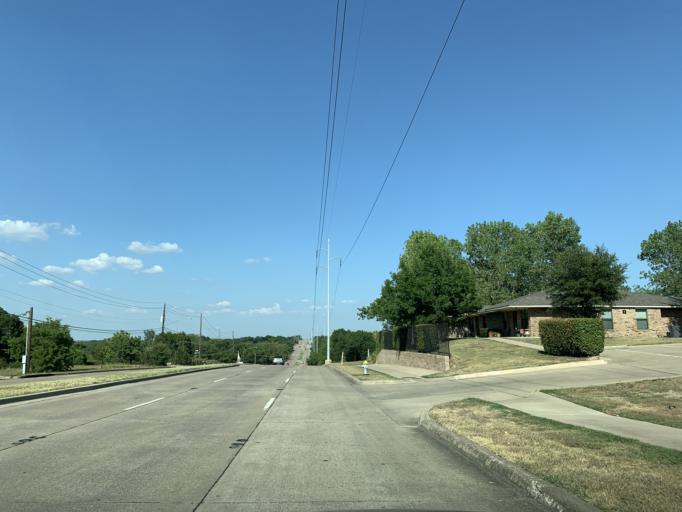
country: US
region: Texas
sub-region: Dallas County
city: Hutchins
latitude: 32.6646
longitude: -96.7795
